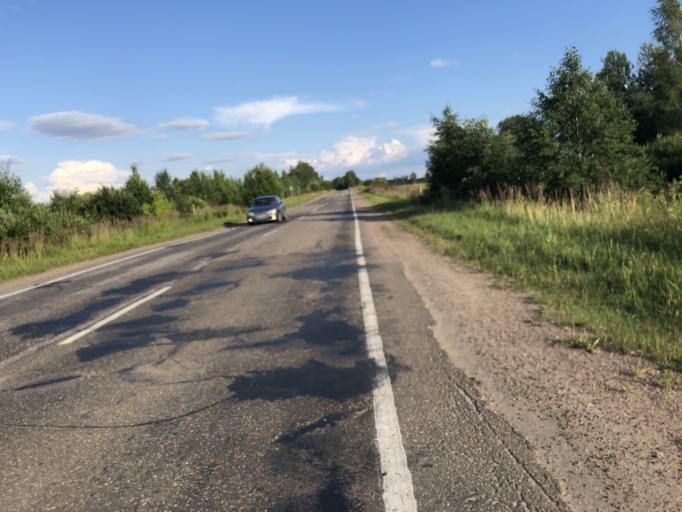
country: RU
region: Tverskaya
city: Rzhev
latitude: 56.2784
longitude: 34.2358
